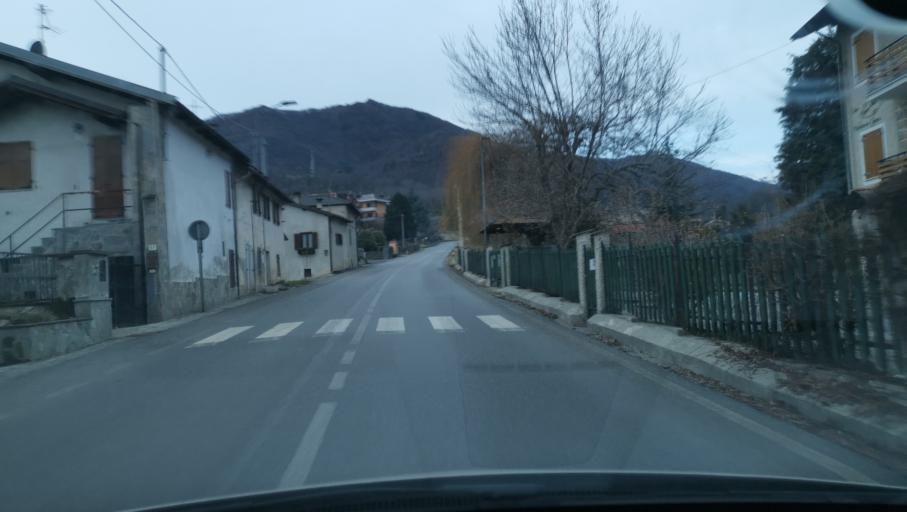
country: IT
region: Piedmont
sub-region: Provincia di Cuneo
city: Monterosso Grana
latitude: 44.4083
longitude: 7.3216
